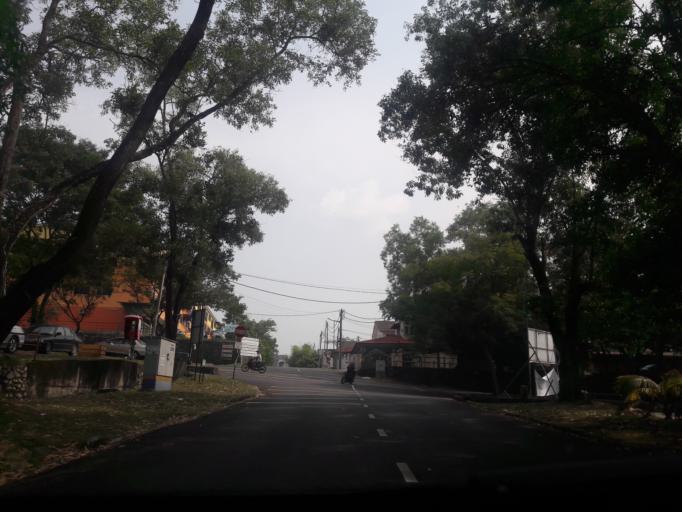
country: MY
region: Kedah
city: Kulim
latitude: 5.3632
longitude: 100.5378
